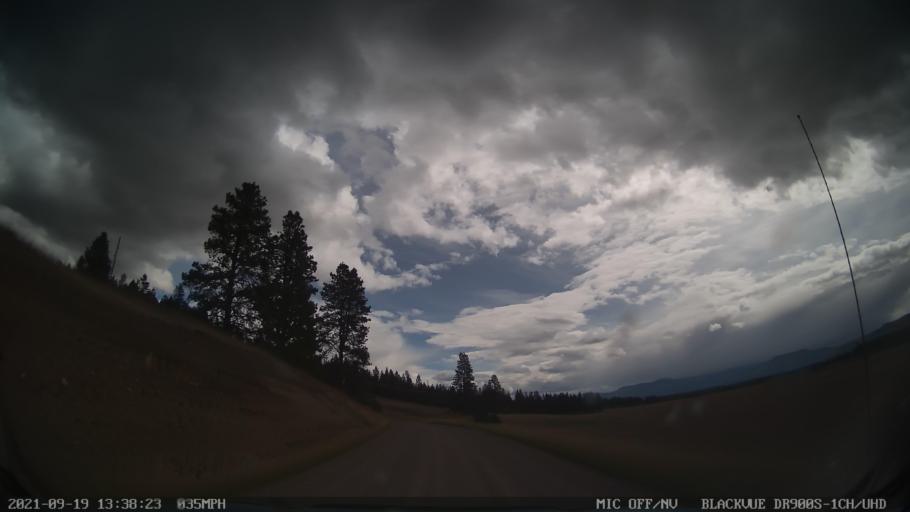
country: US
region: Montana
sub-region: Missoula County
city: Seeley Lake
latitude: 47.1050
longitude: -113.2719
